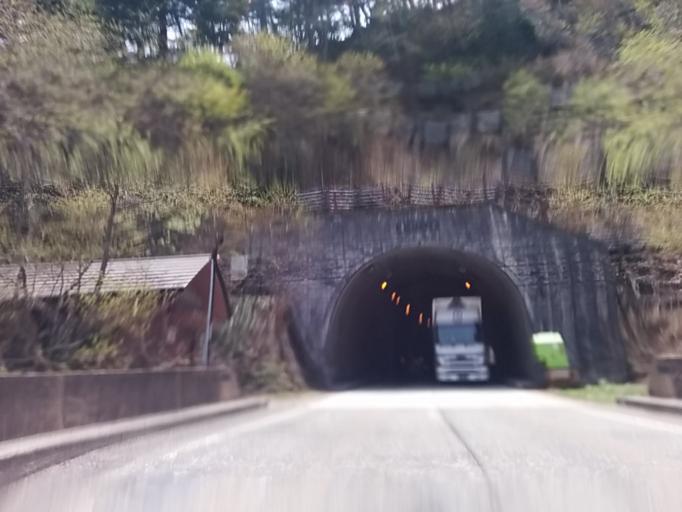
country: JP
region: Gifu
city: Takayama
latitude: 36.1984
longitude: 137.5512
